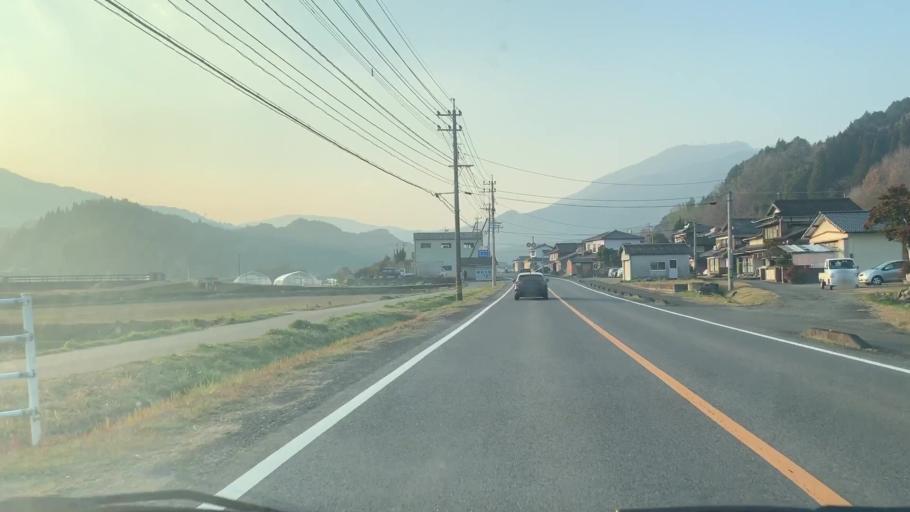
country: JP
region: Saga Prefecture
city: Takeocho-takeo
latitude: 33.2589
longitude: 130.0675
